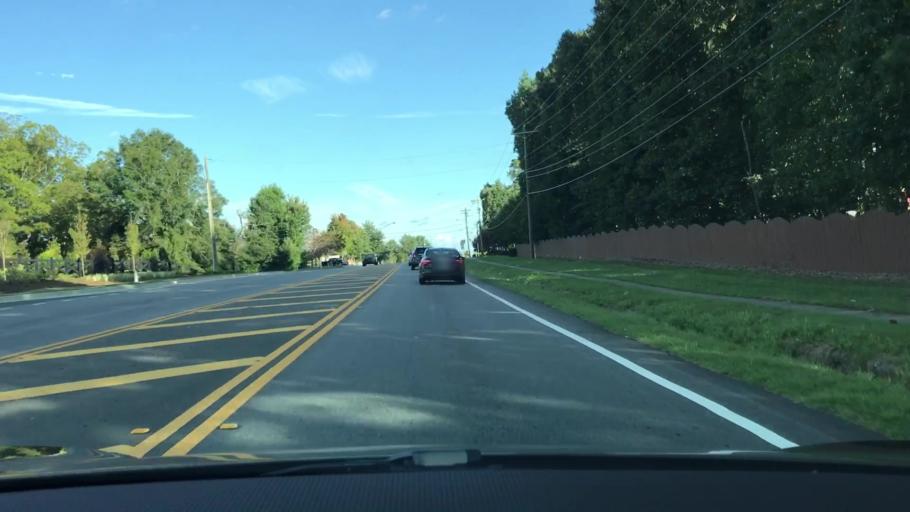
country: US
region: Georgia
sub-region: Gwinnett County
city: Dacula
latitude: 34.0383
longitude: -83.9139
